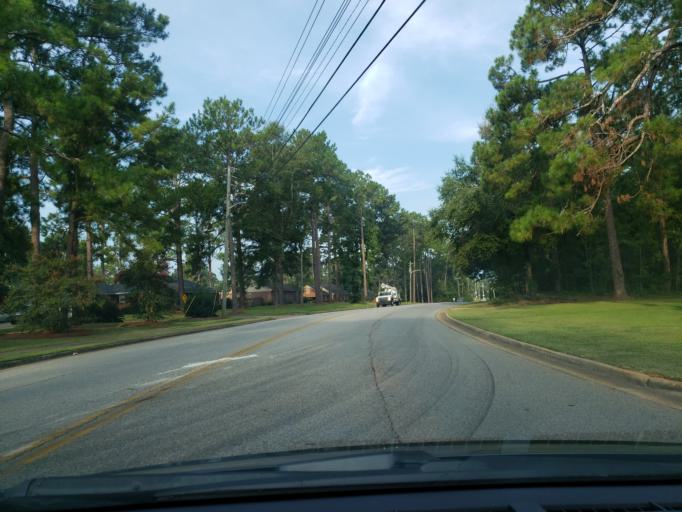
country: US
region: Georgia
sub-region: Dougherty County
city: Albany
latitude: 31.5996
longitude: -84.2157
